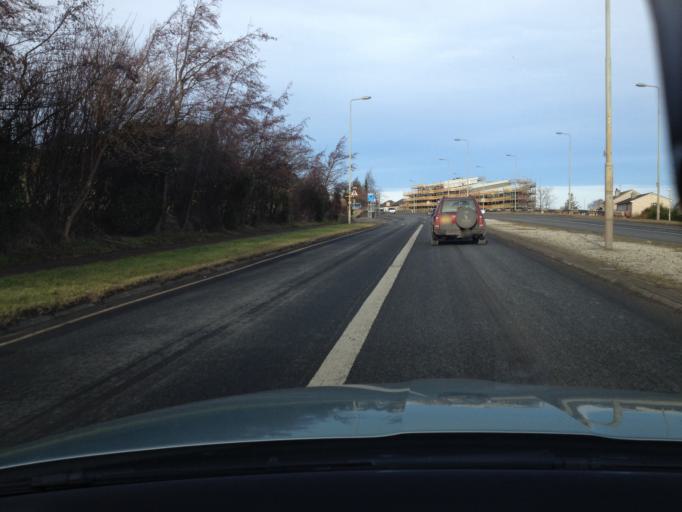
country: GB
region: Scotland
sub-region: Midlothian
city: Loanhead
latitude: 55.8966
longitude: -3.1615
